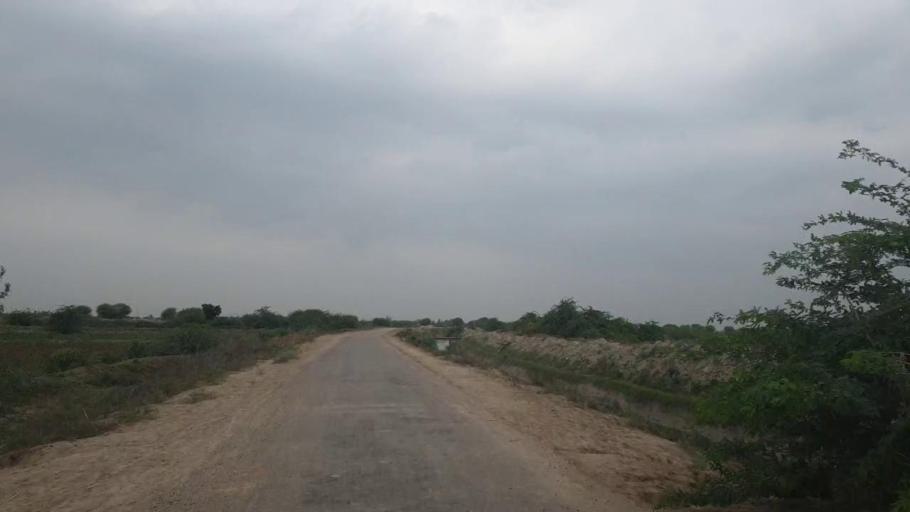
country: PK
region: Sindh
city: Badin
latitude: 24.6260
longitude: 68.6821
